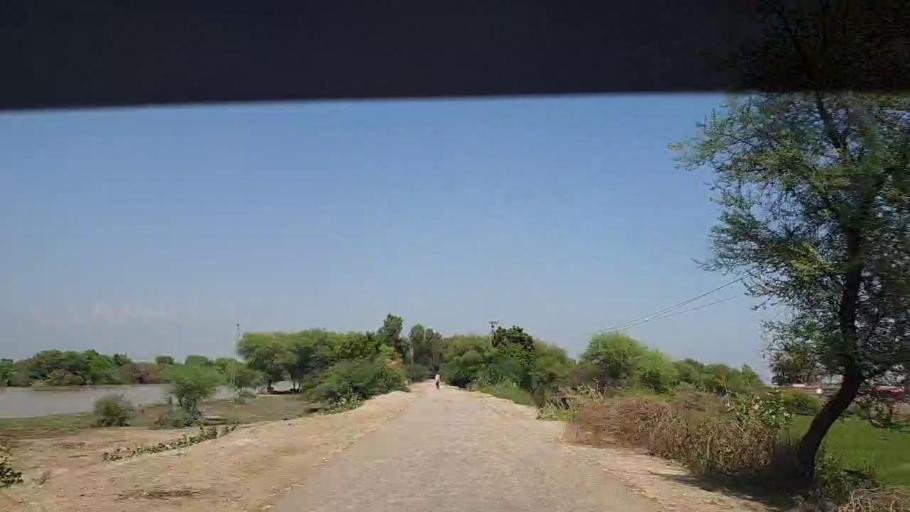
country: PK
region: Sindh
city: Ghauspur
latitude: 28.1662
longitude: 69.1401
